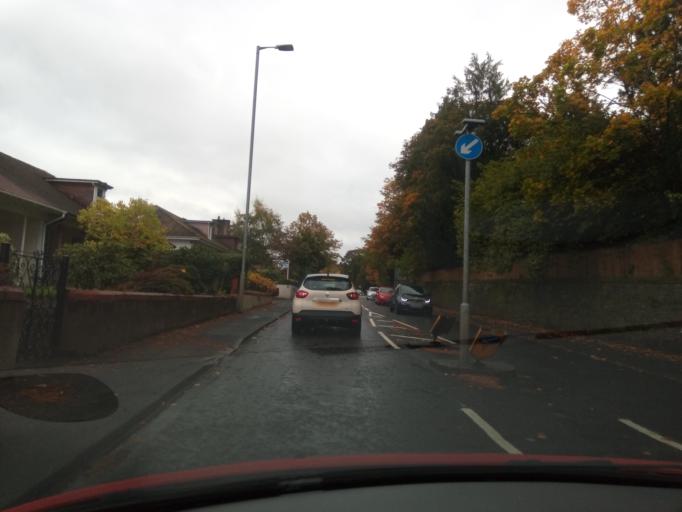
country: GB
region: Scotland
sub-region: The Scottish Borders
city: Galashiels
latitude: 55.6082
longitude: -2.7962
